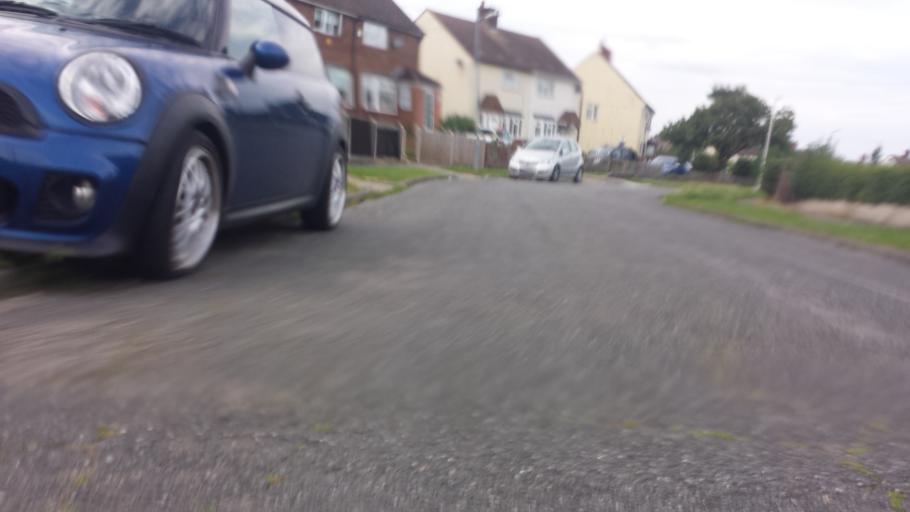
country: GB
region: England
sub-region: Kent
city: Swanley
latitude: 51.3971
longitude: 0.1633
